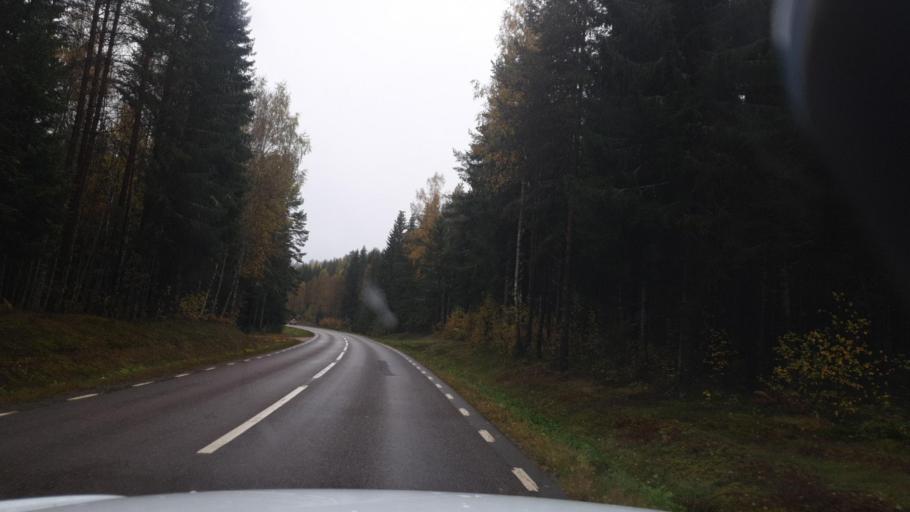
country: SE
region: Vaermland
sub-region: Eda Kommun
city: Amotfors
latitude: 59.6766
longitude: 12.3867
